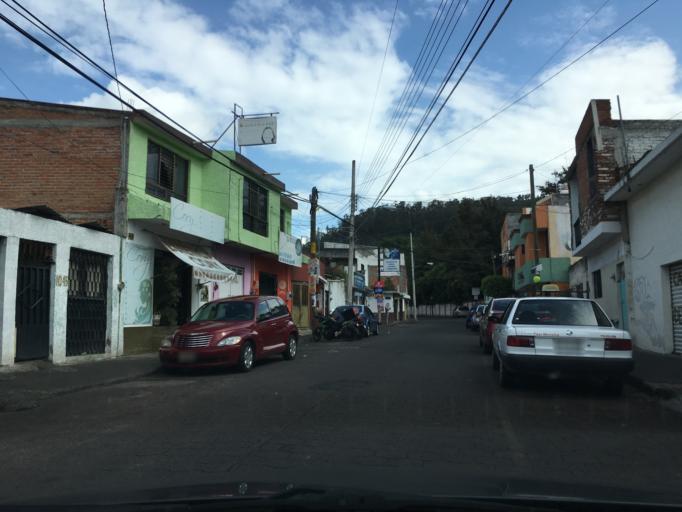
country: MX
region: Michoacan
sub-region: Morelia
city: Montana Monarca (Punta Altozano)
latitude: 19.6854
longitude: -101.1585
